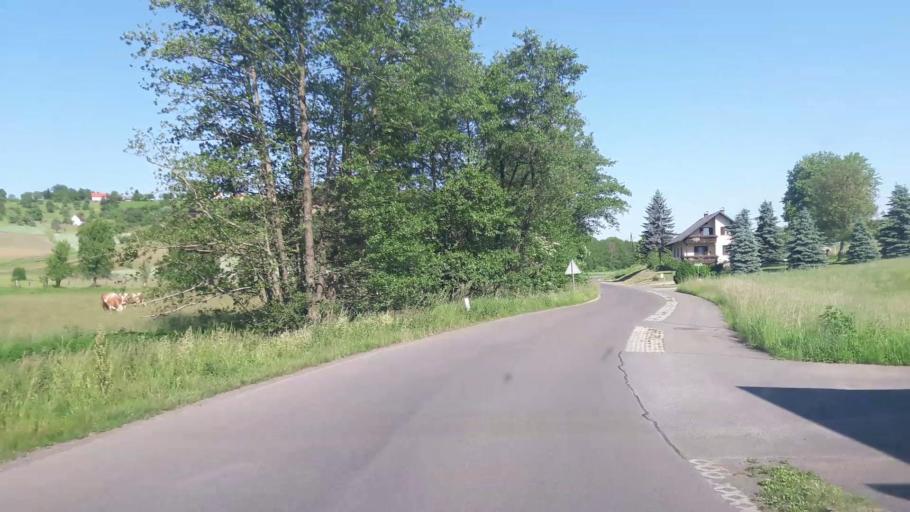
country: AT
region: Styria
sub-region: Politischer Bezirk Suedoststeiermark
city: Unterlamm
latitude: 46.9863
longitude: 16.0464
